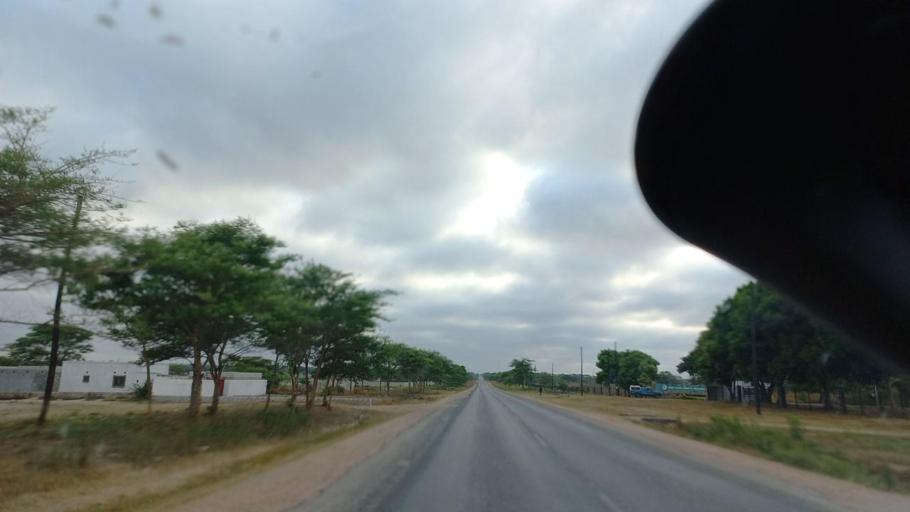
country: ZM
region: Lusaka
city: Chongwe
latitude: -15.3528
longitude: 28.4892
